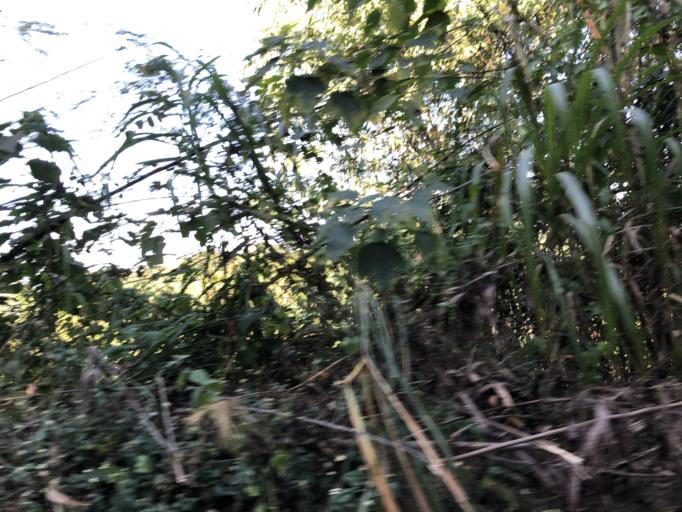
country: TW
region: Taiwan
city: Yujing
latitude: 23.0311
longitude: 120.3829
